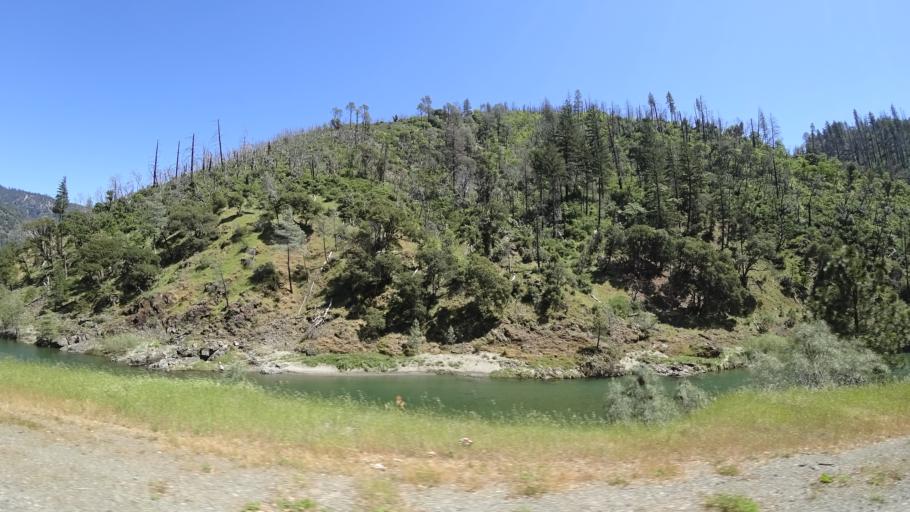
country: US
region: California
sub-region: Humboldt County
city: Willow Creek
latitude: 40.7872
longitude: -123.4175
